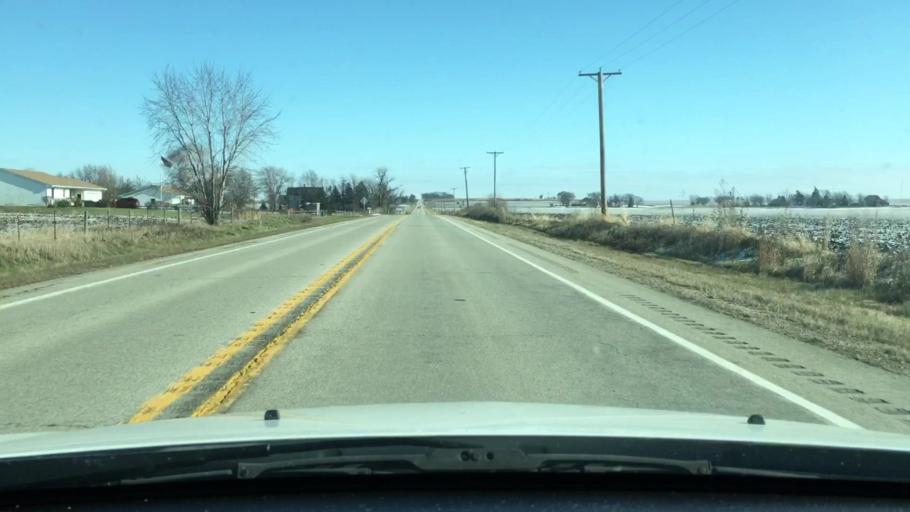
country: US
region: Illinois
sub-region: DeKalb County
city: Malta
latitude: 42.0008
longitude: -88.9306
